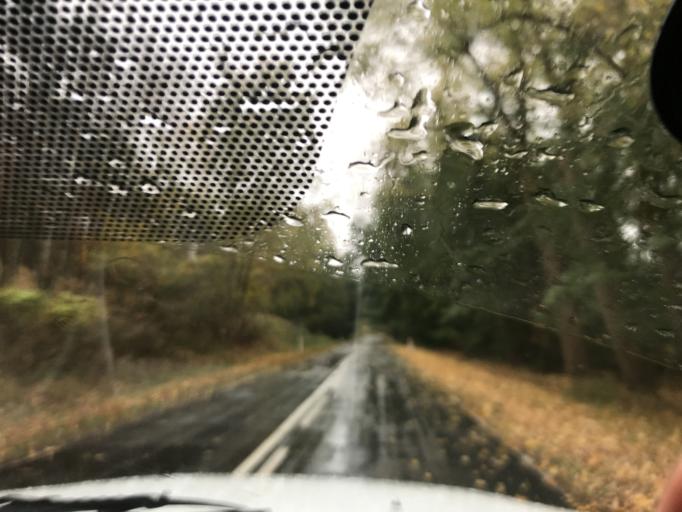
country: DE
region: Brandenburg
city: Neulewin
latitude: 52.7805
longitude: 14.2927
